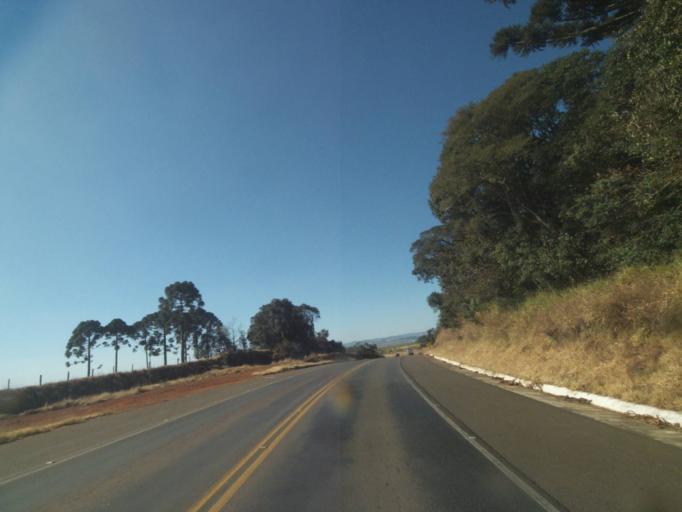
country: BR
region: Parana
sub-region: Tibagi
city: Tibagi
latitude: -24.6960
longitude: -50.4447
